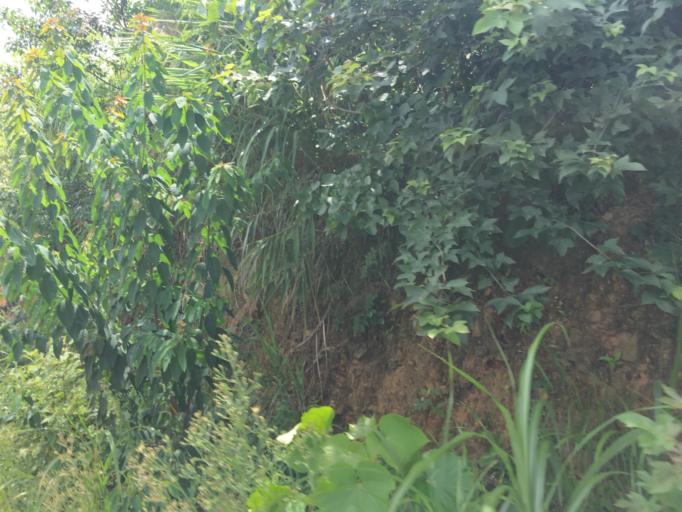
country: CN
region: Guangxi Zhuangzu Zizhiqu
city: Tongle
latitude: 24.9719
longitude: 105.9788
